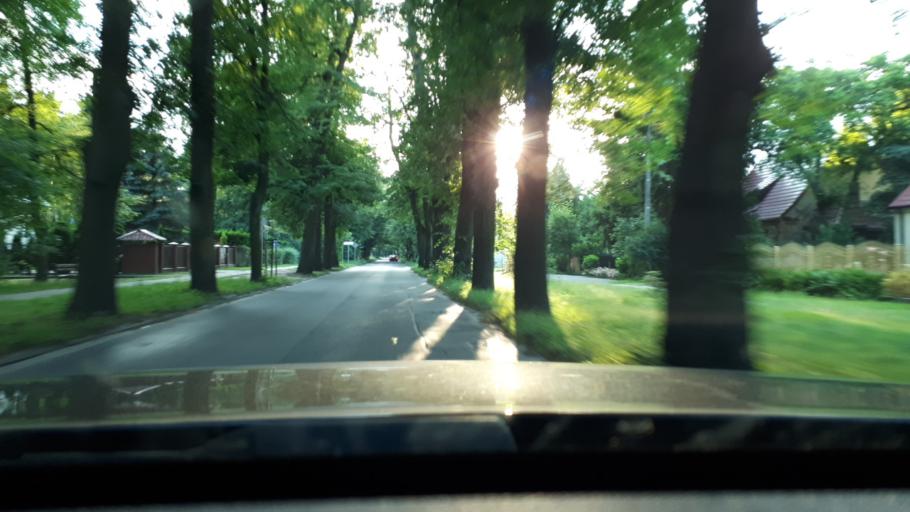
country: PL
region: Masovian Voivodeship
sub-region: Powiat pruszkowski
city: Komorow
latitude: 52.1458
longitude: 20.8219
